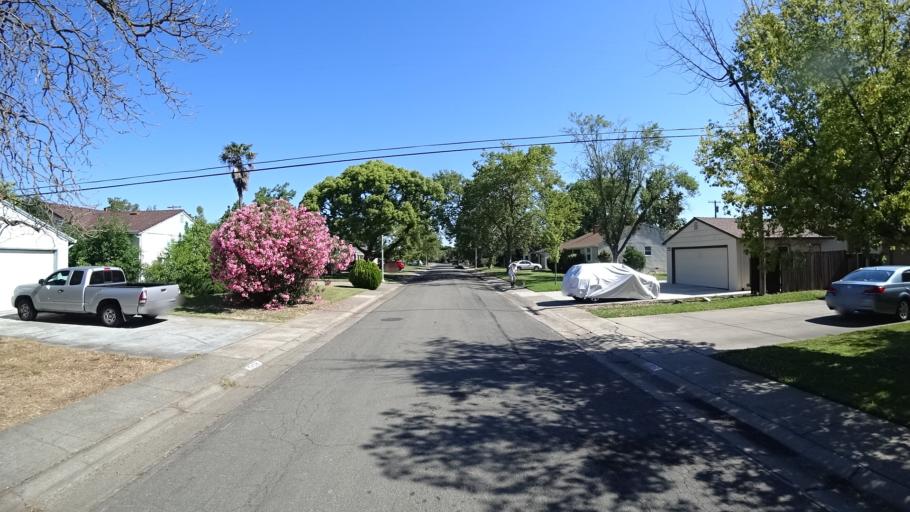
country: US
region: California
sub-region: Sacramento County
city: Parkway
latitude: 38.5262
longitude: -121.4930
